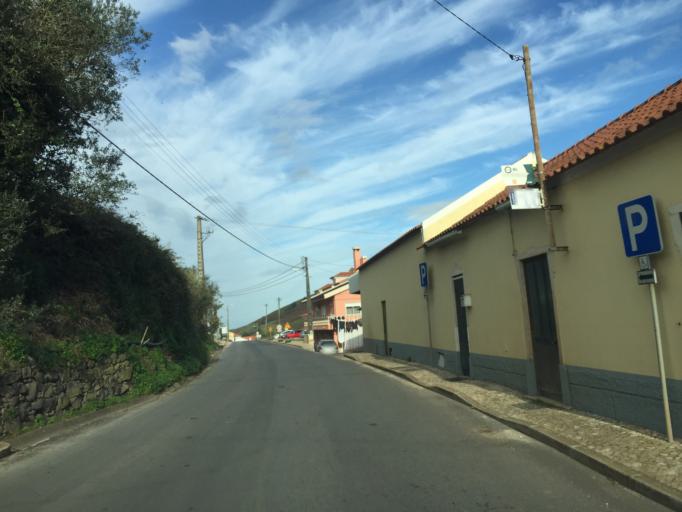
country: PT
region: Lisbon
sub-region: Sintra
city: Almargem
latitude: 38.8486
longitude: -9.2622
